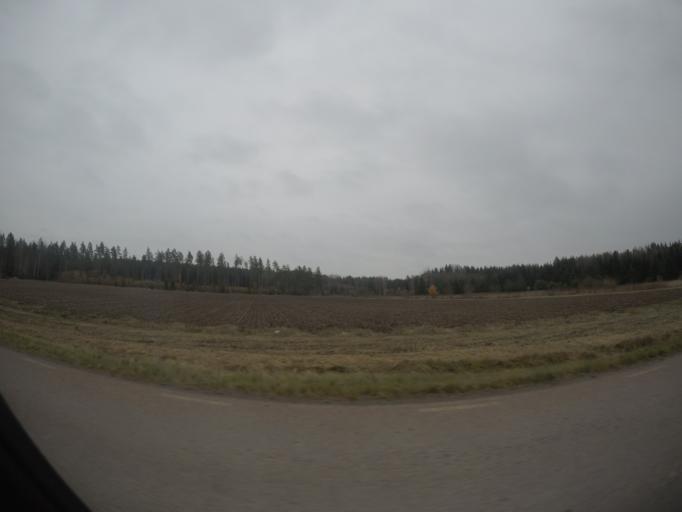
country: SE
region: Vaestmanland
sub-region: Kopings Kommun
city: Koping
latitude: 59.5867
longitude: 16.0864
